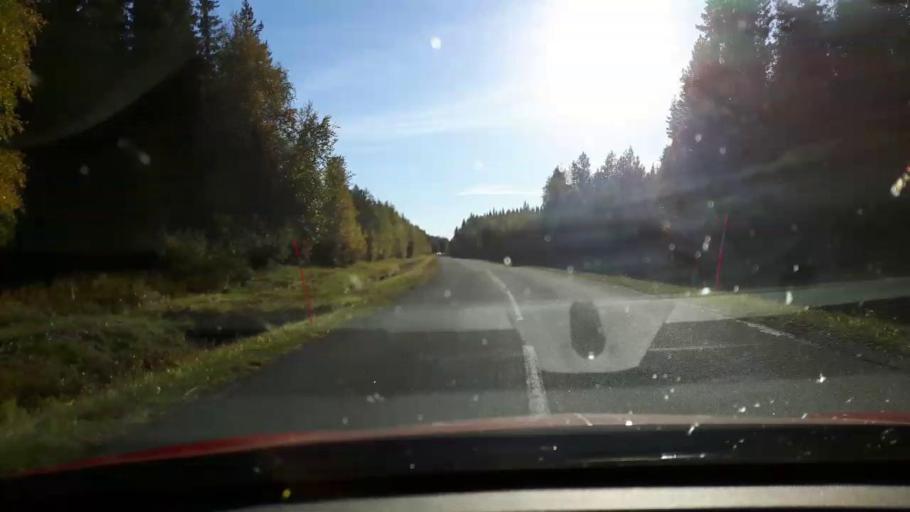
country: SE
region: Jaemtland
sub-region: OEstersunds Kommun
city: Lit
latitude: 63.8269
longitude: 14.8627
